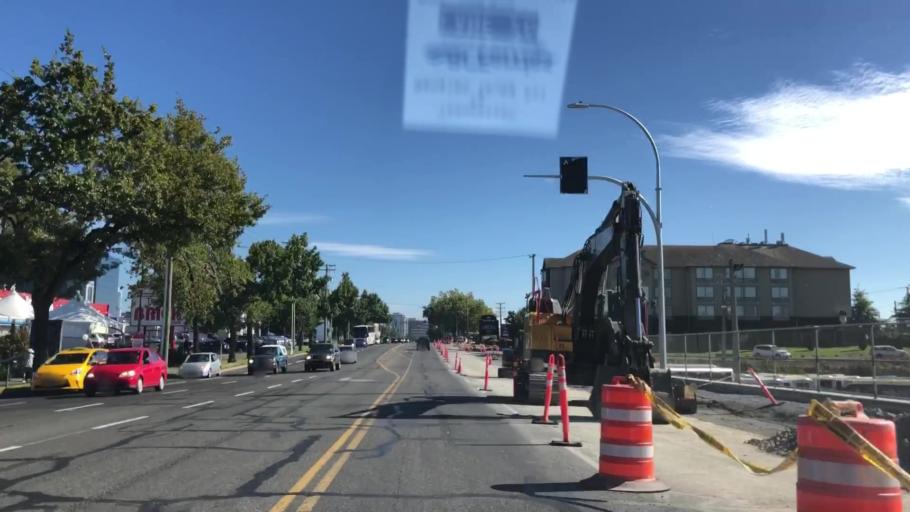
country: CA
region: British Columbia
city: Victoria
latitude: 48.4409
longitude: -123.3684
